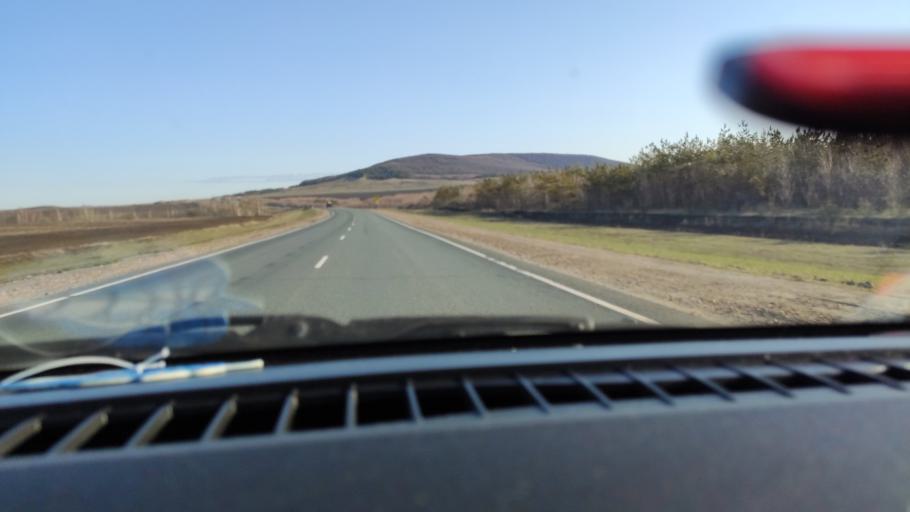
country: RU
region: Saratov
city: Alekseyevka
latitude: 52.2792
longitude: 47.9317
